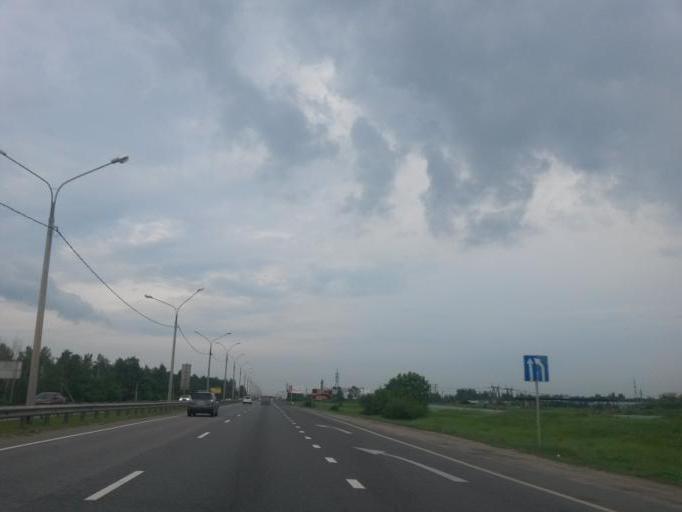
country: RU
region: Moskovskaya
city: Yam
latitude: 55.4685
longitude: 37.7497
